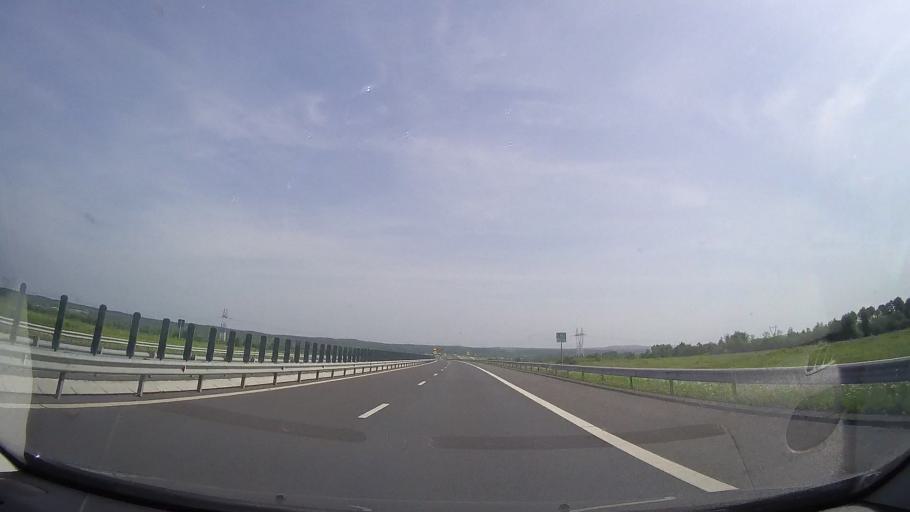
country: RO
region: Timis
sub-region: Comuna Margina
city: Margina
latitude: 45.8497
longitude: 22.2366
